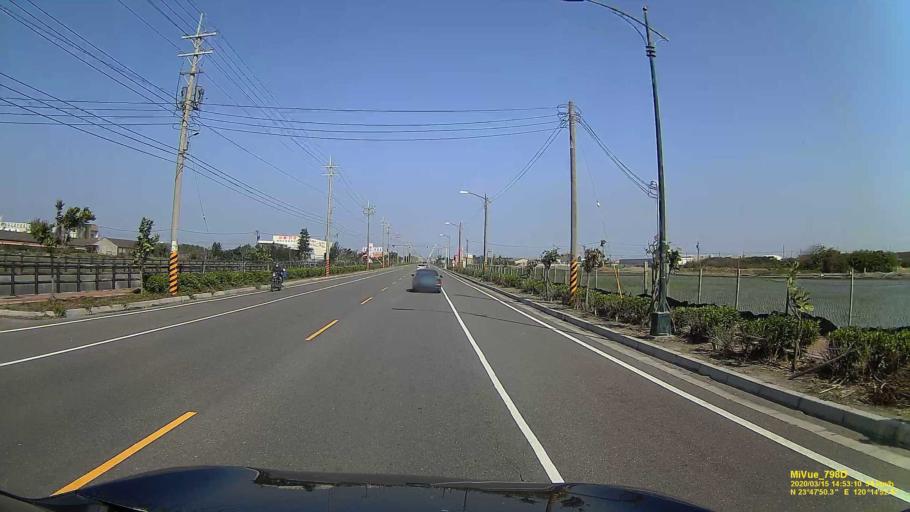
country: TW
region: Taiwan
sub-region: Yunlin
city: Douliu
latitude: 23.7973
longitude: 120.2481
